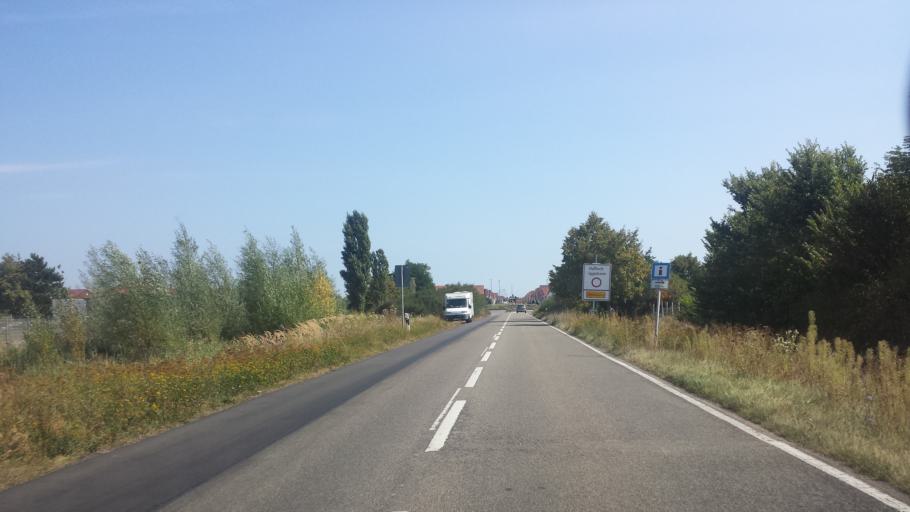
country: DE
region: Rheinland-Pfalz
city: Hassloch
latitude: 49.3633
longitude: 8.2347
